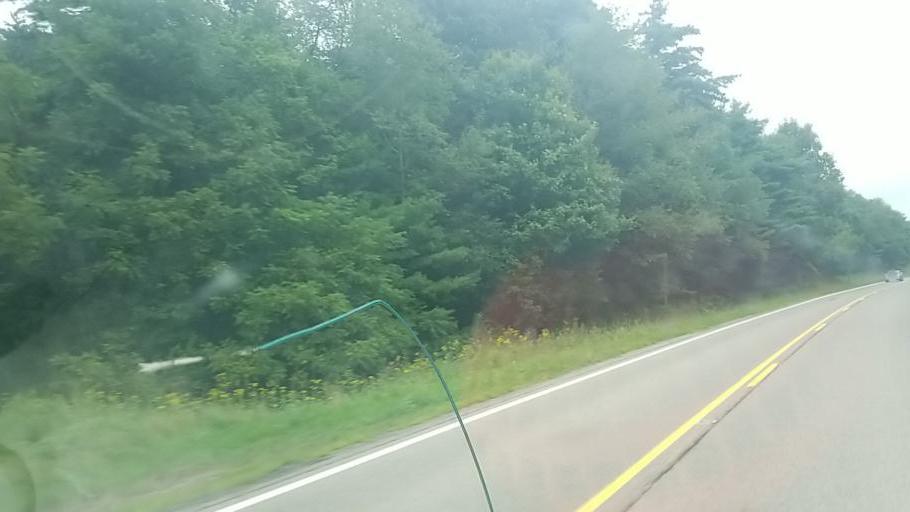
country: US
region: Ohio
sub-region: Knox County
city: Danville
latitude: 40.4613
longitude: -82.2146
